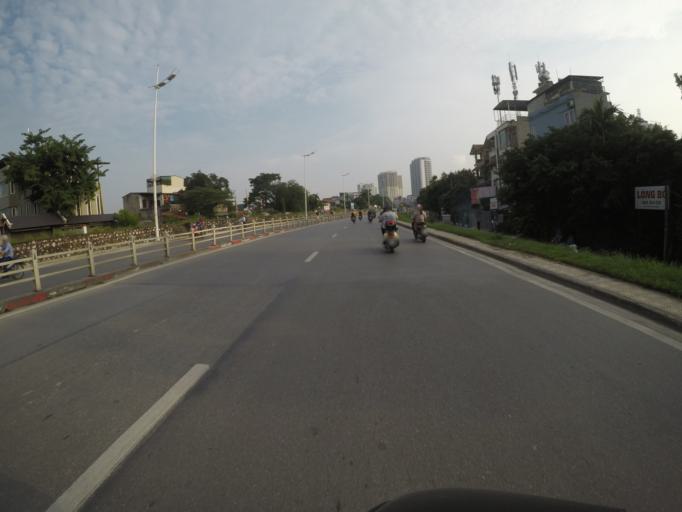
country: VN
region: Ha Noi
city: Tay Ho
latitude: 21.0720
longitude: 105.8259
